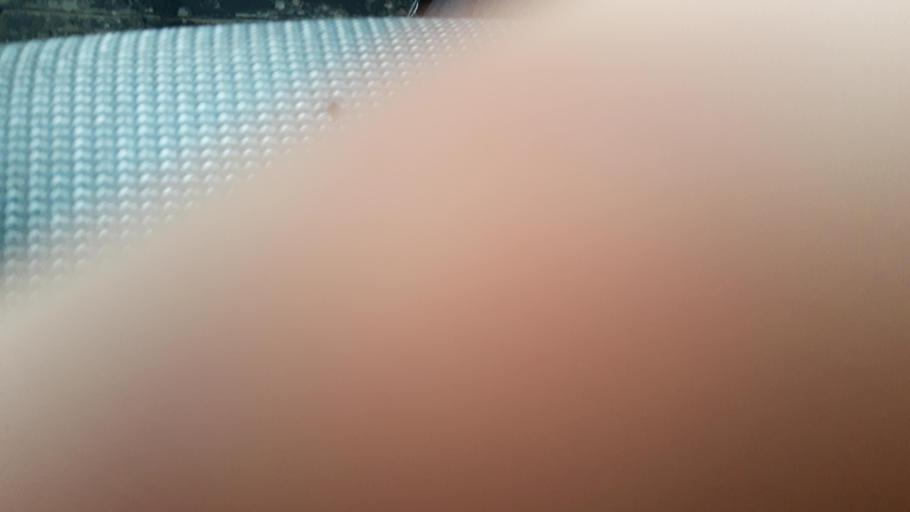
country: RU
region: Bashkortostan
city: Ufa
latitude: 54.8452
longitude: 56.0013
